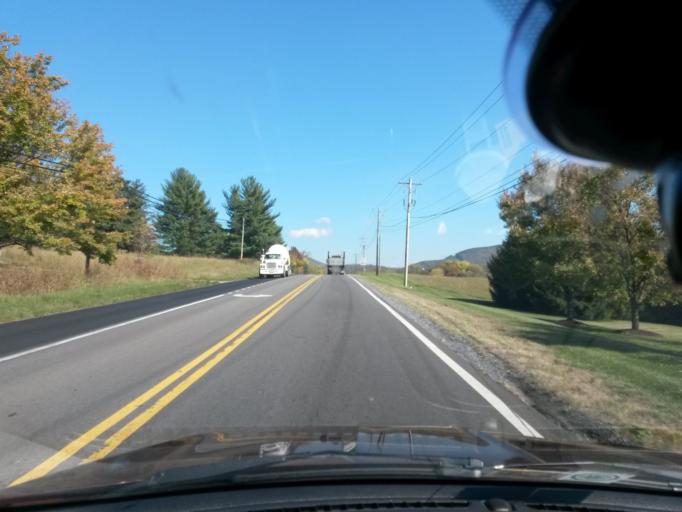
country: US
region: Virginia
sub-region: Botetourt County
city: Cloverdale
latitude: 37.3644
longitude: -79.9168
